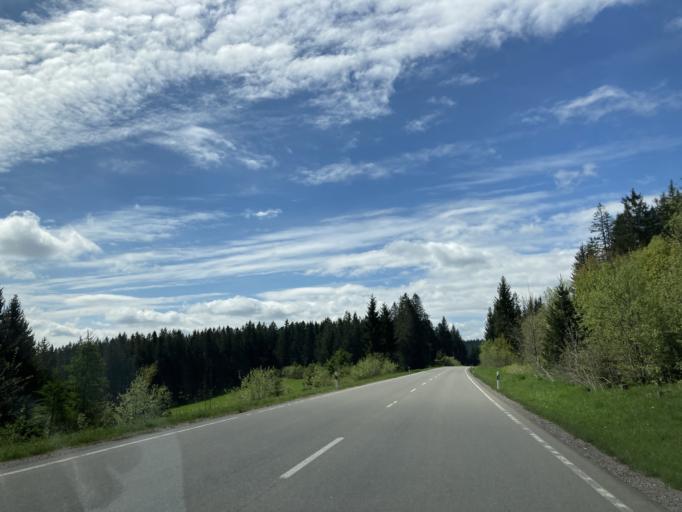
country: DE
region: Baden-Wuerttemberg
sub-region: Freiburg Region
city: Furtwangen im Schwarzwald
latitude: 48.0106
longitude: 8.2036
